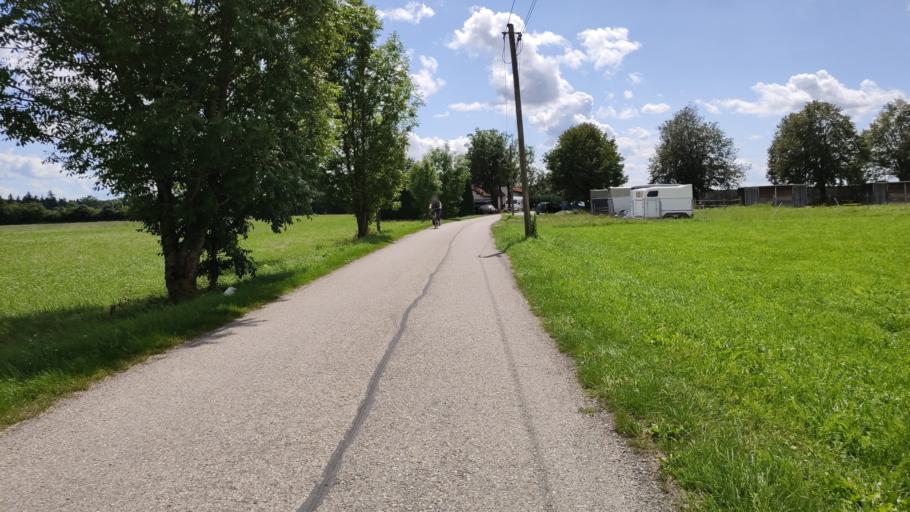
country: DE
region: Bavaria
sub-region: Swabia
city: Konigsbrunn
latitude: 48.2352
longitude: 10.8938
